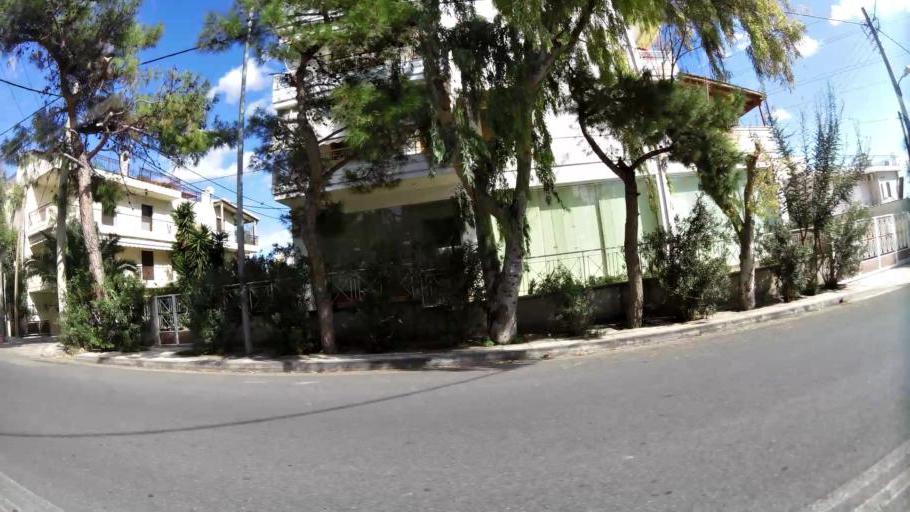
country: GR
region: Attica
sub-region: Nomarchia Anatolikis Attikis
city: Acharnes
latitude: 38.1013
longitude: 23.7370
